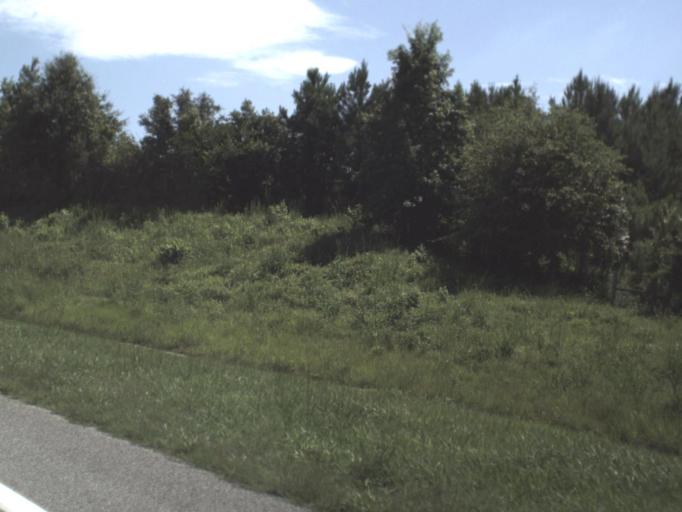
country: US
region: Florida
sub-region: Hamilton County
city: Jasper
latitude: 30.4033
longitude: -82.9339
